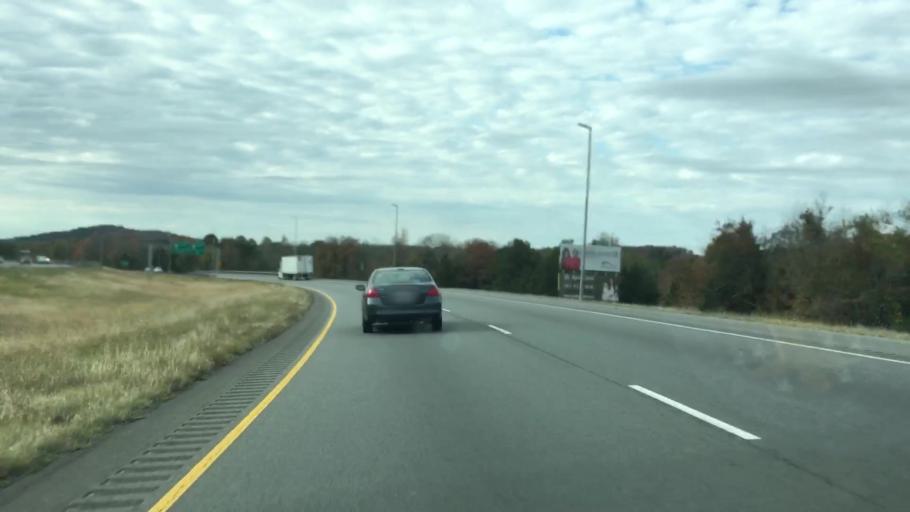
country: US
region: Arkansas
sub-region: Faulkner County
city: Conway
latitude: 35.1181
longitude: -92.4511
